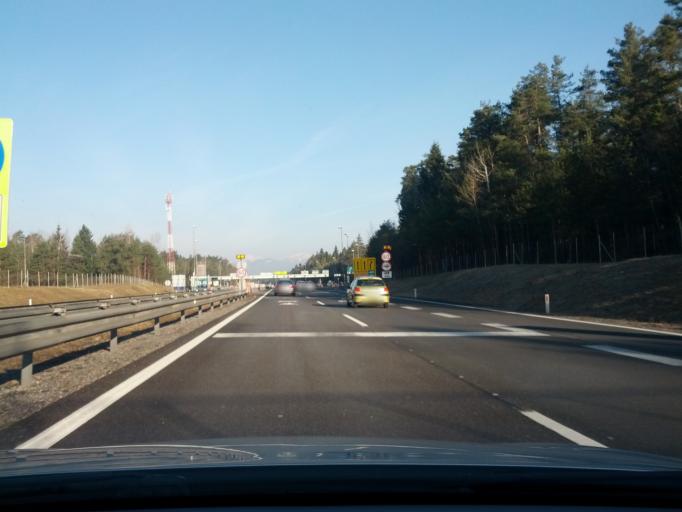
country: SI
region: Vodice
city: Vodice
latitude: 46.1933
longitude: 14.4751
